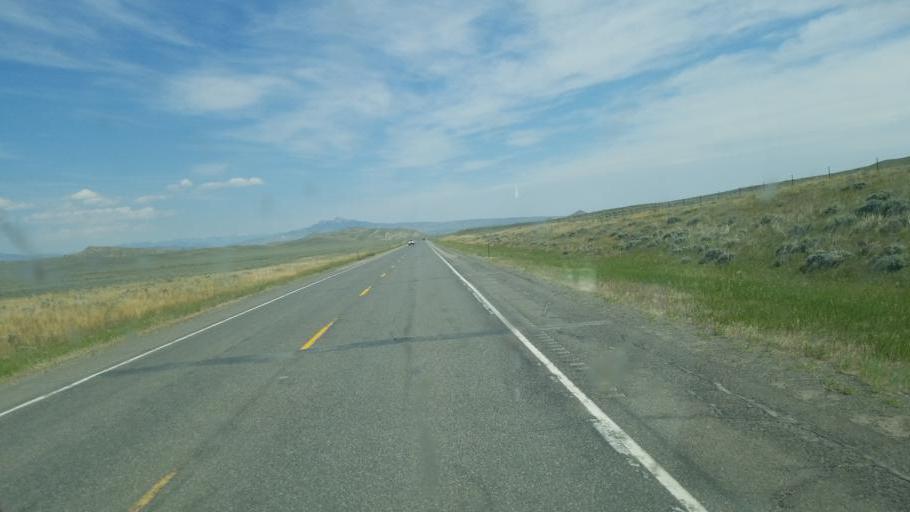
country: US
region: Wyoming
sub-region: Park County
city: Cody
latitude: 44.4378
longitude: -109.0136
